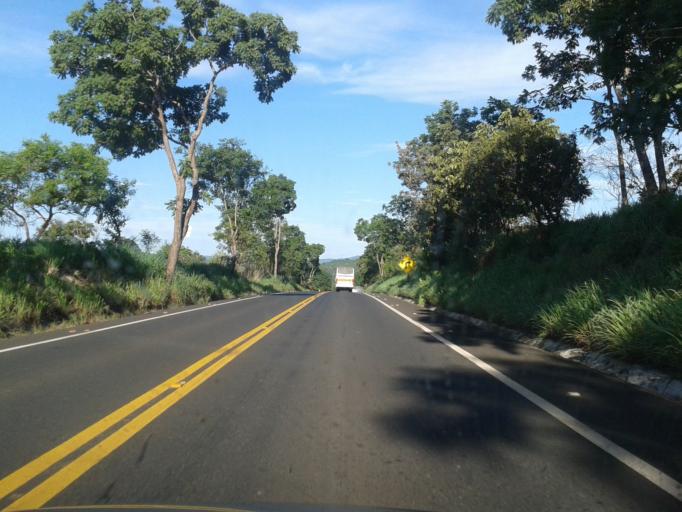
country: BR
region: Goias
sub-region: Caldas Novas
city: Caldas Novas
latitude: -18.1139
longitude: -48.6112
